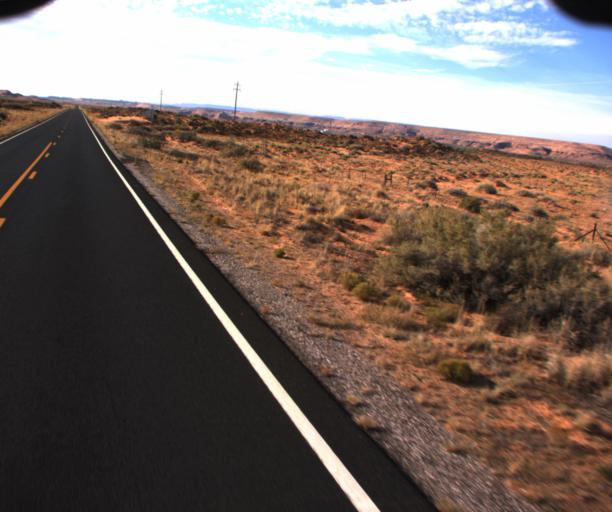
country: US
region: Arizona
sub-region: Apache County
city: Many Farms
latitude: 36.8112
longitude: -109.6470
